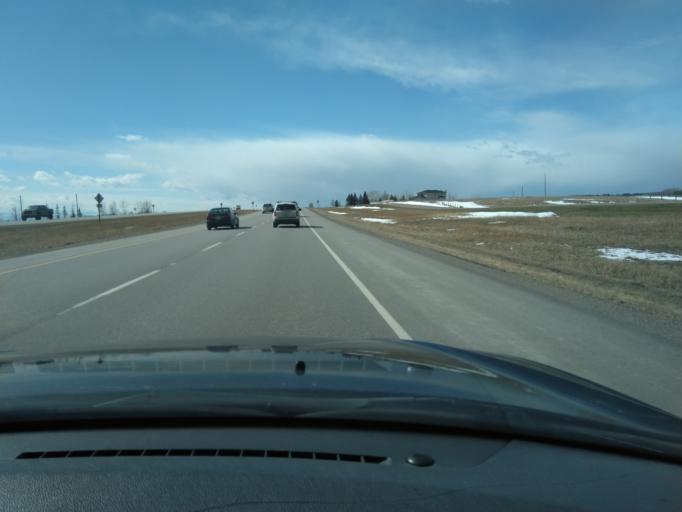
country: CA
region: Alberta
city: Cochrane
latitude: 51.1605
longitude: -114.2872
